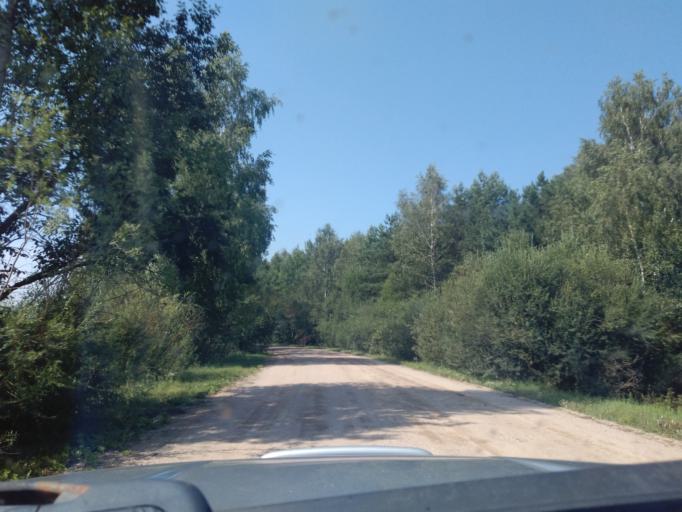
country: BY
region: Minsk
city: Valozhyn
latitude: 54.0112
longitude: 26.5959
